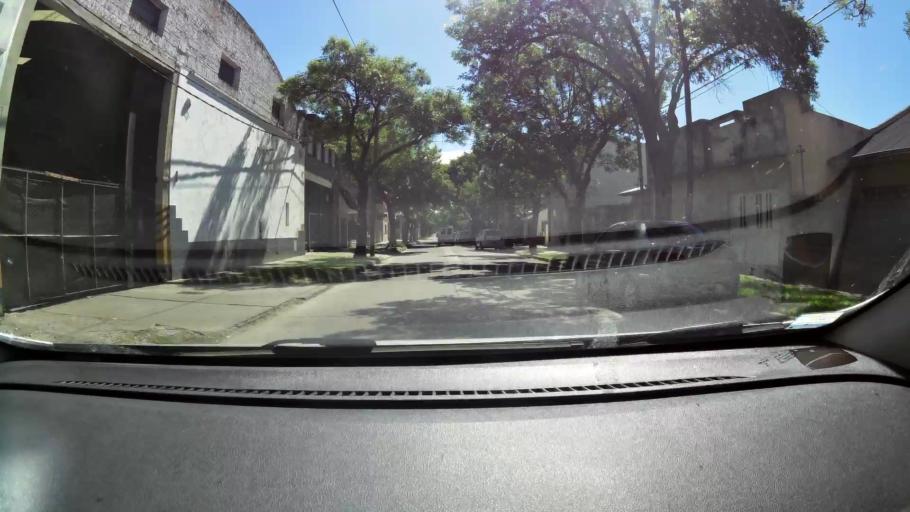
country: AR
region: Santa Fe
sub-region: Departamento de Rosario
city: Rosario
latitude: -32.9386
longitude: -60.6966
